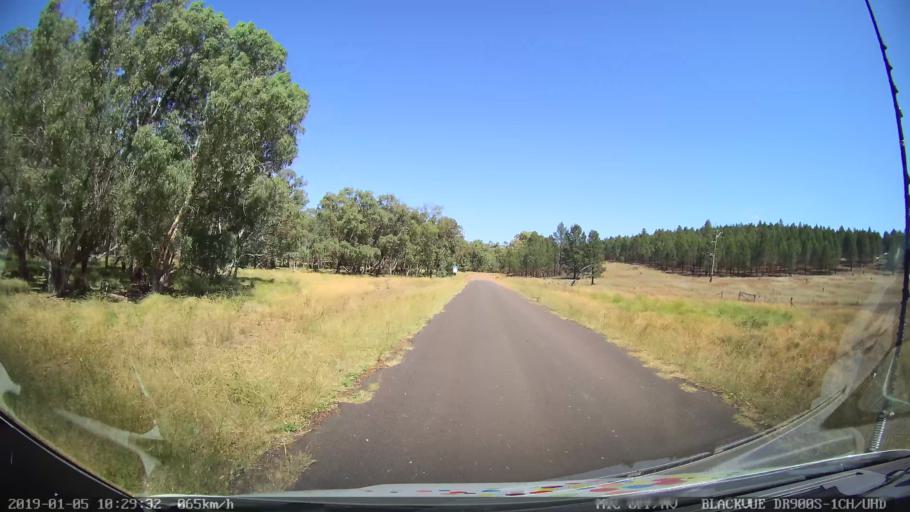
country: AU
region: New South Wales
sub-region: Gilgandra
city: Gilgandra
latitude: -31.5394
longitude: 148.9291
